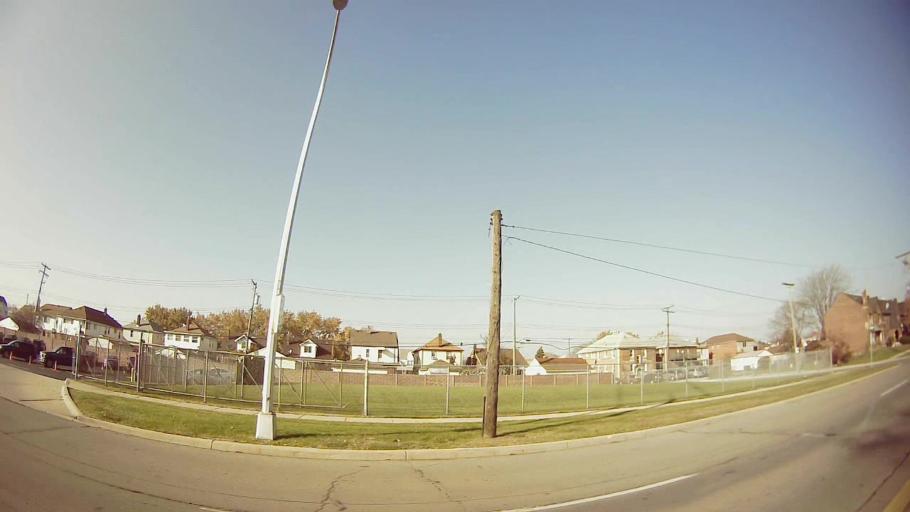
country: US
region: Michigan
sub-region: Wayne County
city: Dearborn
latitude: 42.3312
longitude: -83.1665
